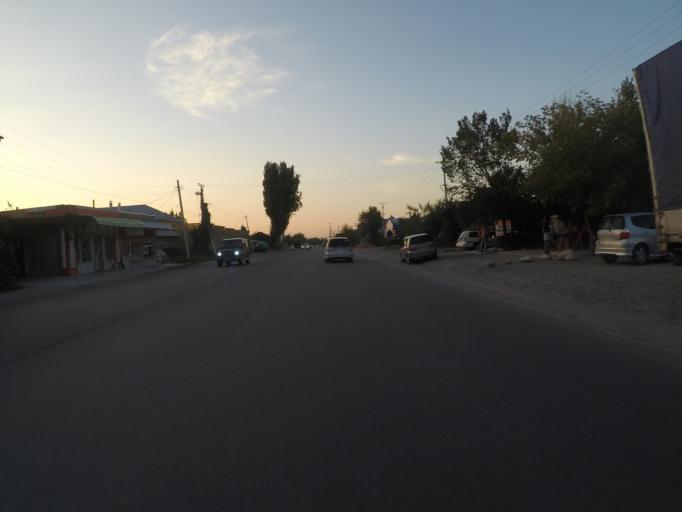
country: KG
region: Chuy
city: Lebedinovka
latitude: 42.8088
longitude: 74.6467
